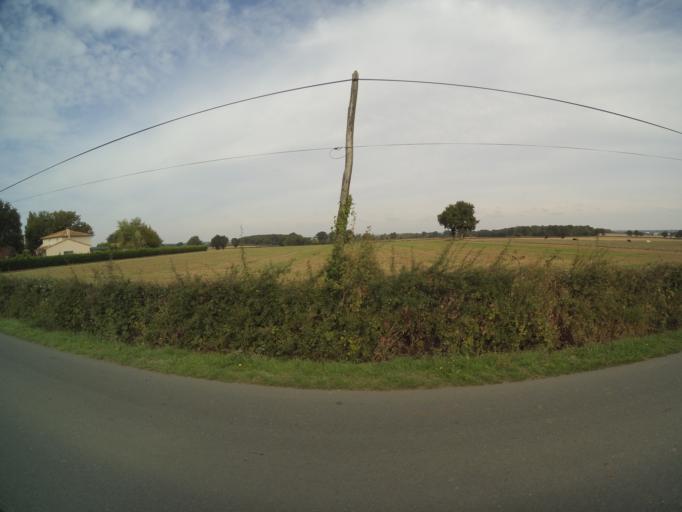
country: FR
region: Pays de la Loire
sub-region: Departement de Maine-et-Loire
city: Chemille-Melay
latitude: 47.2108
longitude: -0.6988
